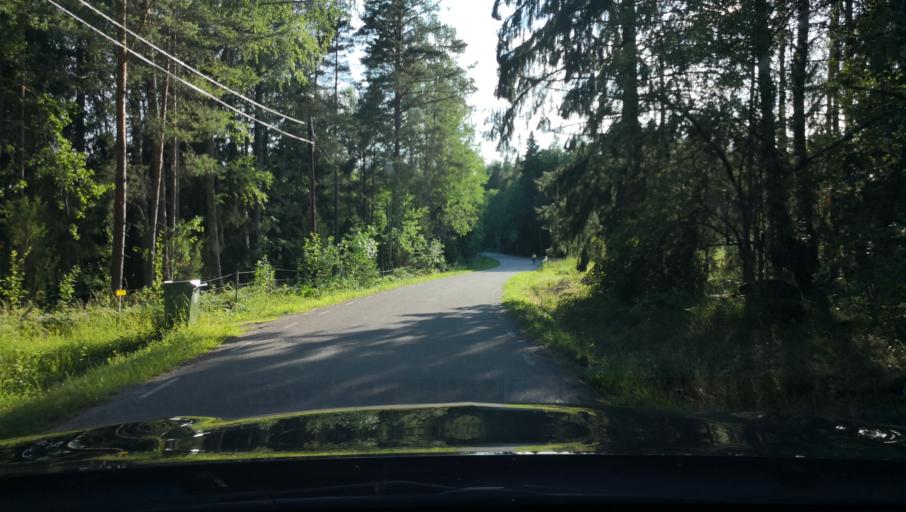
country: SE
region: Uppsala
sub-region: Osthammars Kommun
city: Osterbybruk
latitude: 60.0190
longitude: 17.9431
